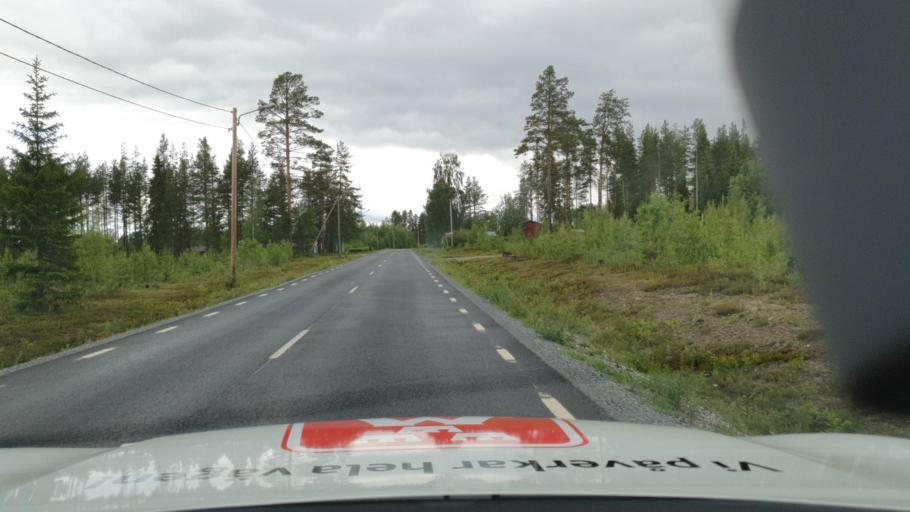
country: SE
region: Vaesterbotten
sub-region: Dorotea Kommun
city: Dorotea
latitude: 64.2163
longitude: 16.5481
